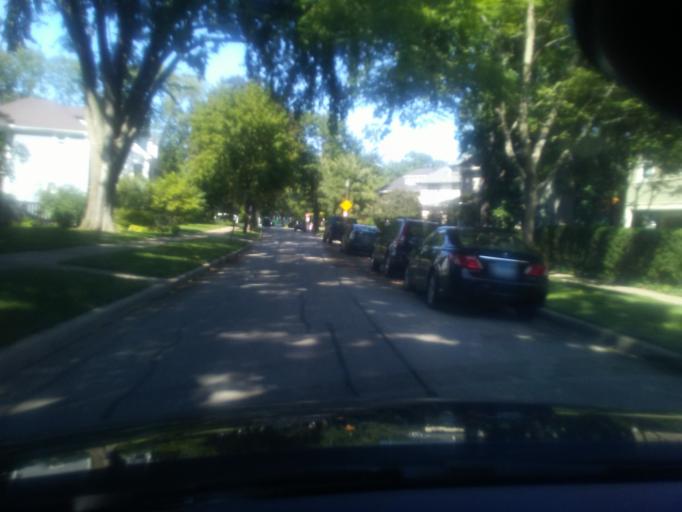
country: US
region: Illinois
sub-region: Cook County
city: Wilmette
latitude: 42.0625
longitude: -87.7048
